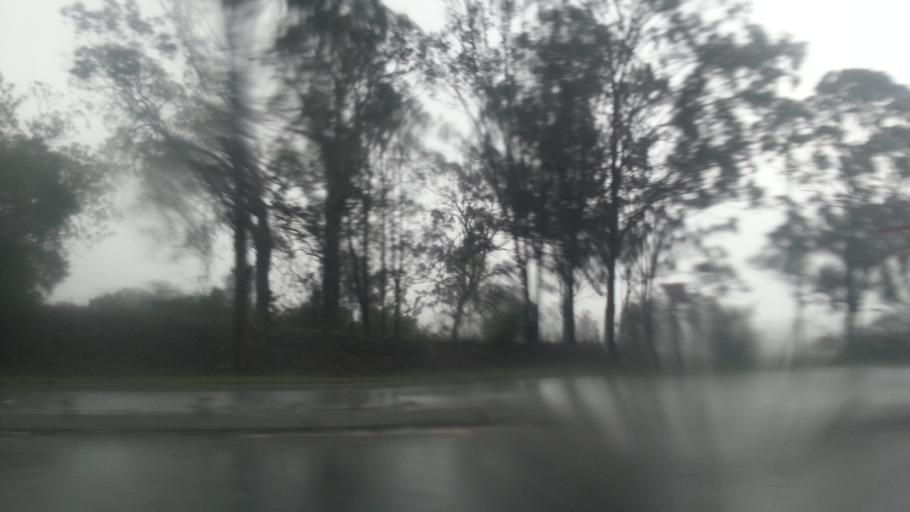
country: AU
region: New South Wales
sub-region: Camden
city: Camden South
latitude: -34.0974
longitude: 150.6953
